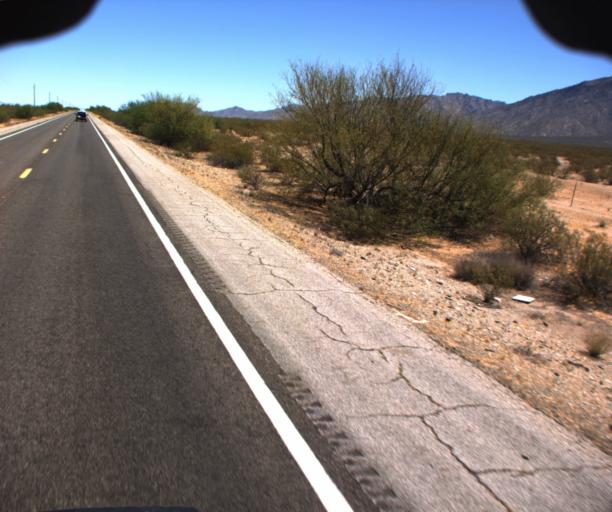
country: US
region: Arizona
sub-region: La Paz County
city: Salome
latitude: 33.8571
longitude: -113.4311
